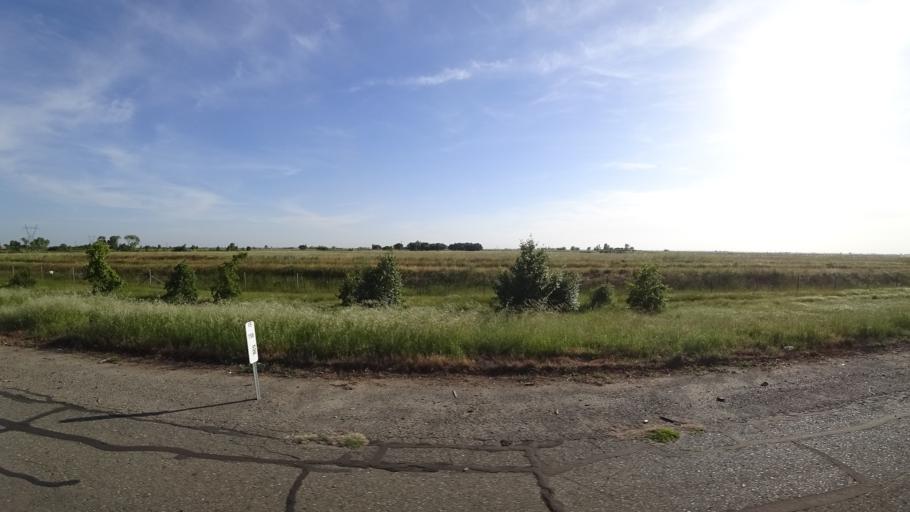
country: US
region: California
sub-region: Yuba County
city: Wheatland
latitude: 39.0459
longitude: -121.4868
